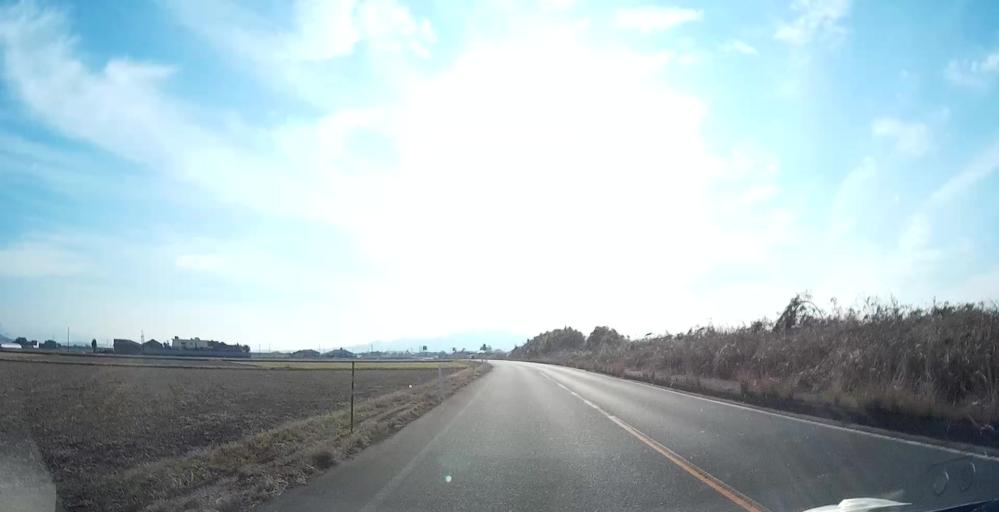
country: JP
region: Kumamoto
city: Uto
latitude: 32.7373
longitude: 130.6652
